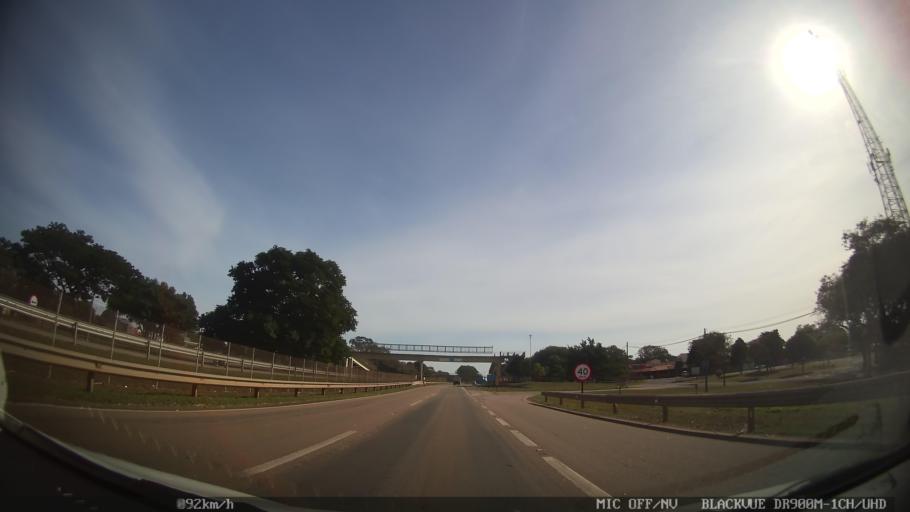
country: BR
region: Sao Paulo
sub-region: Rio Das Pedras
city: Rio das Pedras
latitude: -22.7734
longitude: -47.5923
